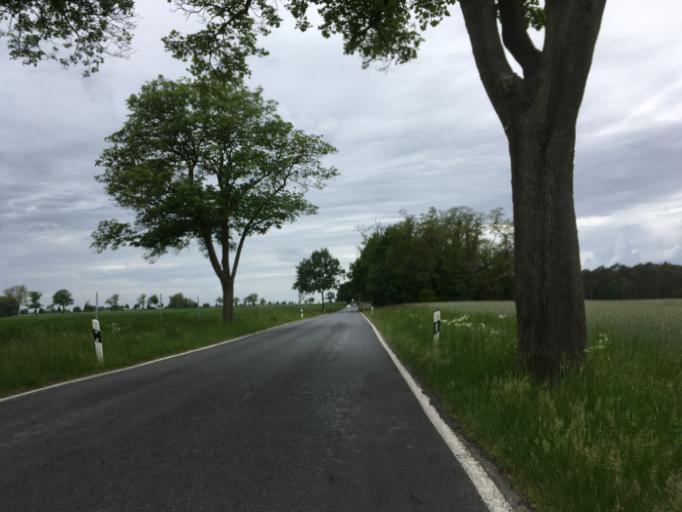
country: DE
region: Brandenburg
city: Bernau bei Berlin
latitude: 52.6684
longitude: 13.6394
